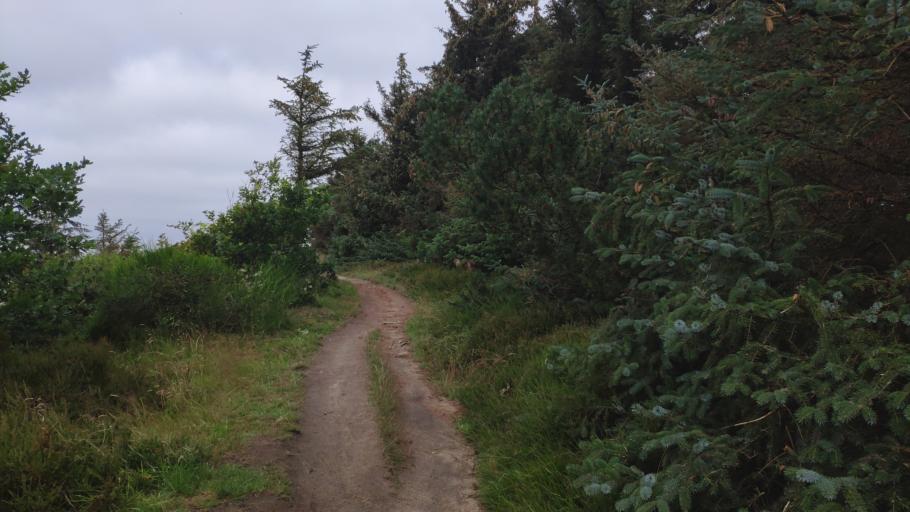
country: DK
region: South Denmark
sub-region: Varde Kommune
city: Oksbol
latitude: 55.5367
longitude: 8.3355
